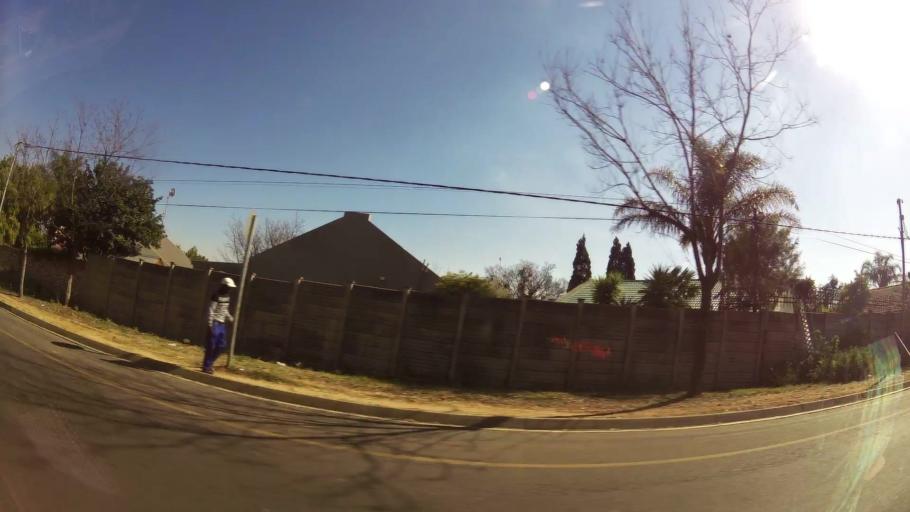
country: ZA
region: Gauteng
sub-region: City of Tshwane Metropolitan Municipality
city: Centurion
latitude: -25.8462
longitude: 28.2010
